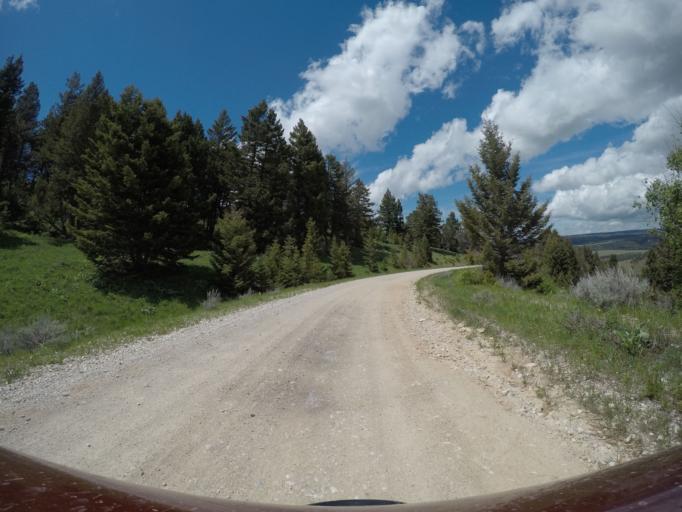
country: US
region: Wyoming
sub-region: Big Horn County
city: Lovell
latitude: 45.1916
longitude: -108.4797
